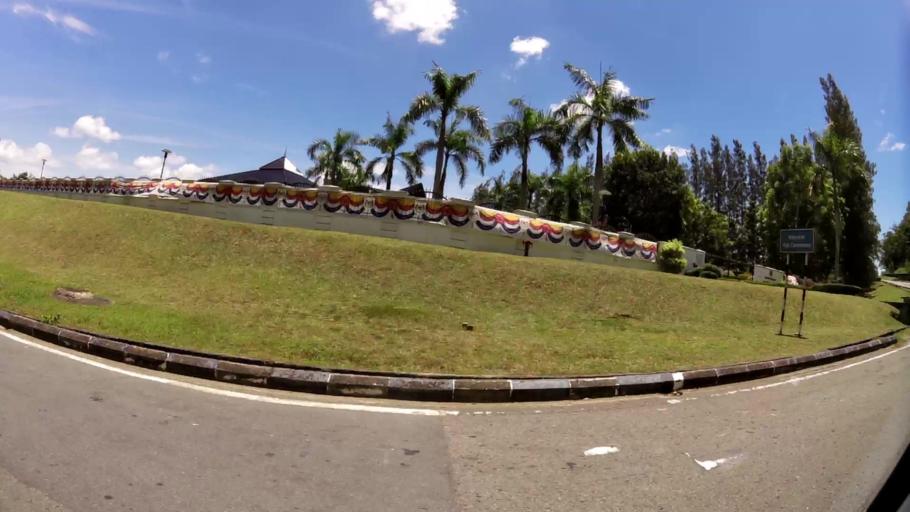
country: BN
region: Brunei and Muara
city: Bandar Seri Begawan
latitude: 4.9217
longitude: 114.9594
